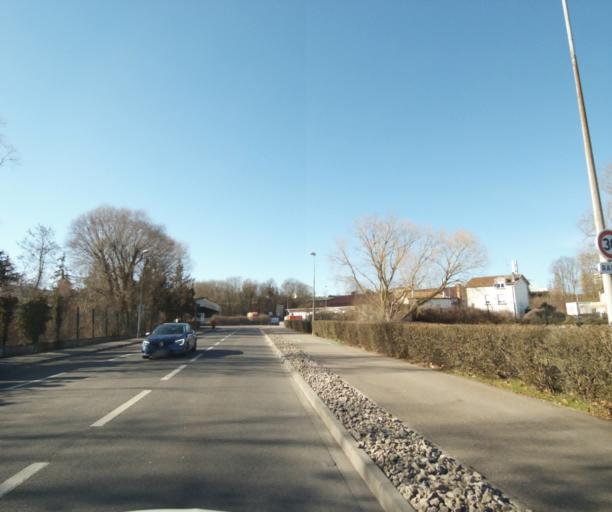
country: FR
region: Lorraine
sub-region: Departement de Meurthe-et-Moselle
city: Vandoeuvre-les-Nancy
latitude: 48.6567
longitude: 6.1887
